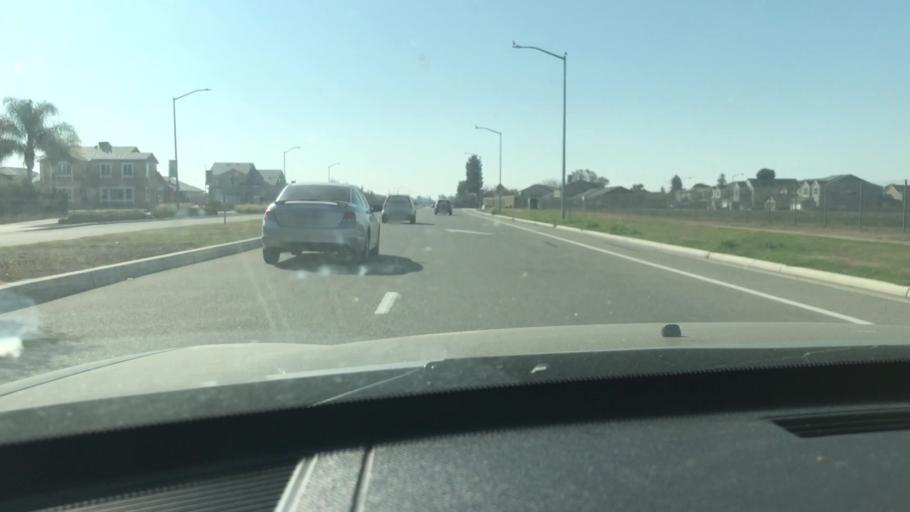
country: US
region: California
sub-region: Fresno County
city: Tarpey Village
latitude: 36.7910
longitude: -119.6641
